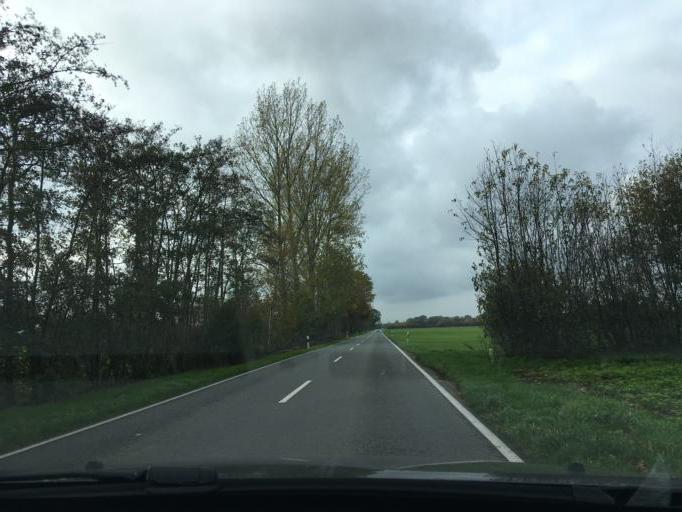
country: NL
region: Overijssel
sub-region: Gemeente Haaksbergen
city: Haaksbergen
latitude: 52.0694
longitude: 6.7352
